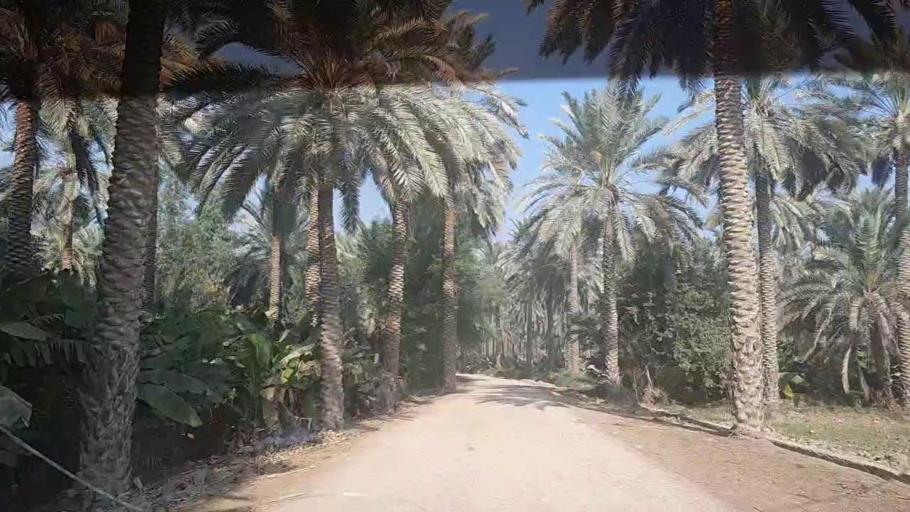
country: PK
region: Sindh
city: Khairpur
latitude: 27.4653
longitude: 68.7171
